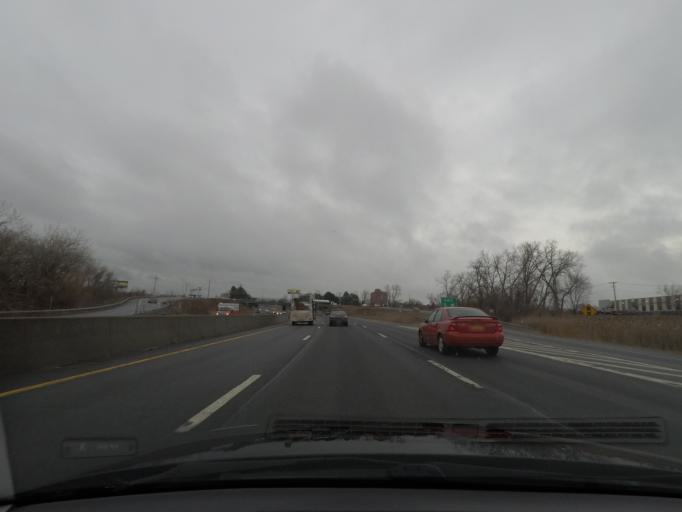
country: US
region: New York
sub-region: Albany County
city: West Albany
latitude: 42.6835
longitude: -73.7876
